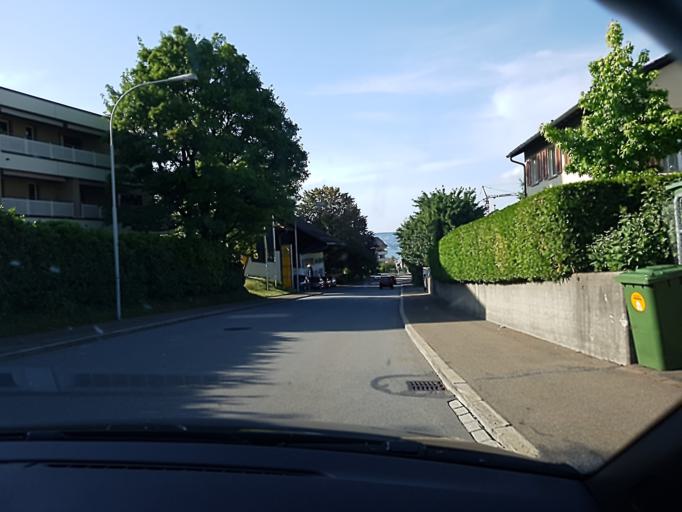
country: CH
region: Zurich
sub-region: Bezirk Horgen
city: Thalwil / Nord
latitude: 47.2948
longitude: 8.5597
